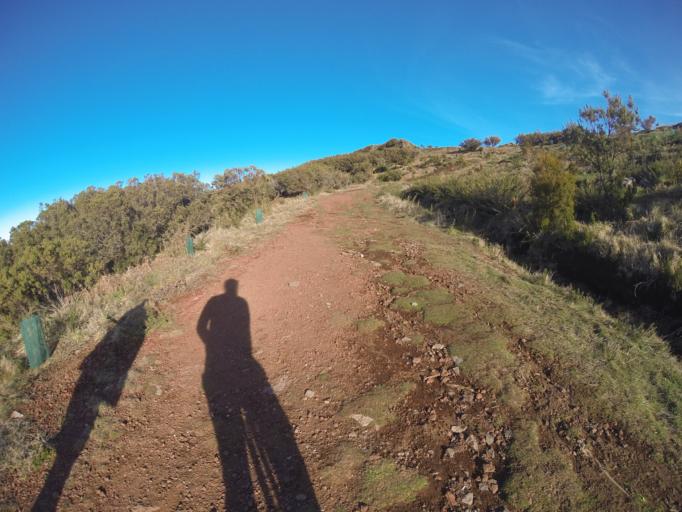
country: PT
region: Madeira
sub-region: Sao Vicente
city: Sao Vicente
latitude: 32.7567
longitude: -17.0573
